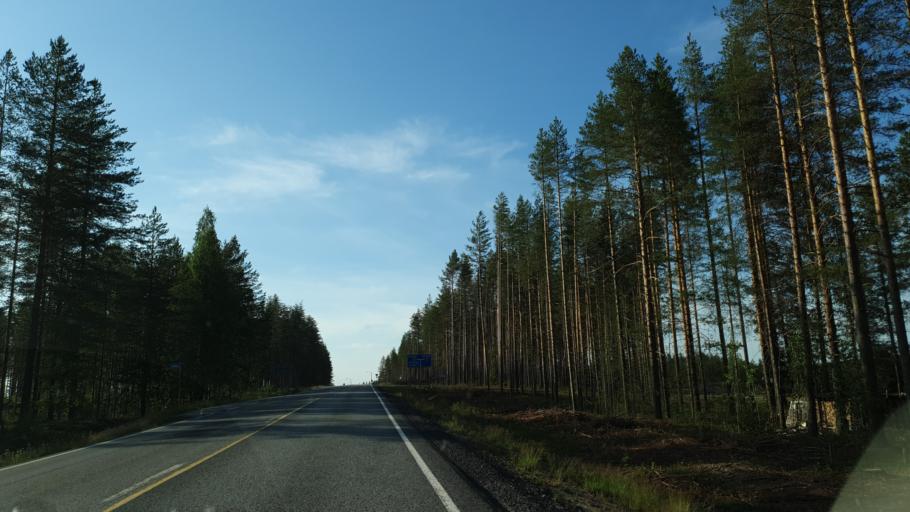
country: FI
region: Kainuu
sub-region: Kehys-Kainuu
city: Kuhmo
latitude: 64.0957
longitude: 29.4773
